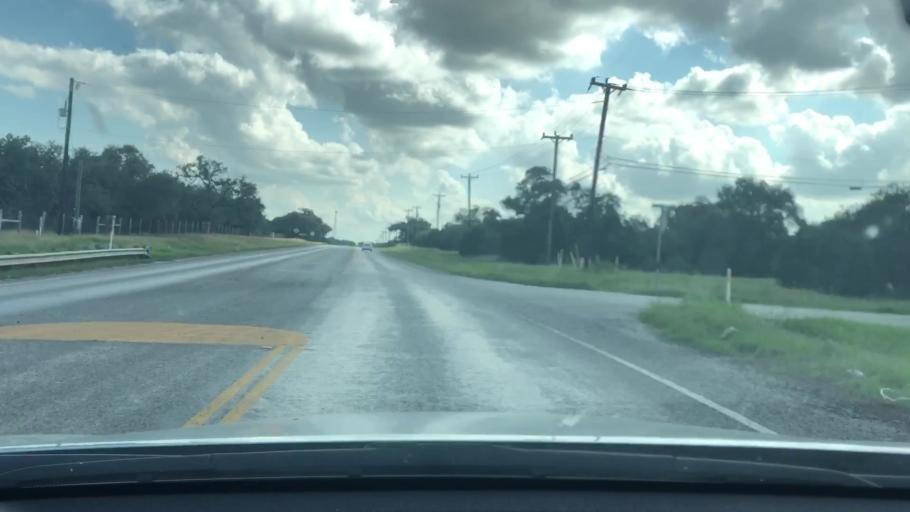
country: US
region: Texas
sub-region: Bexar County
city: Fair Oaks Ranch
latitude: 29.7525
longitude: -98.6235
